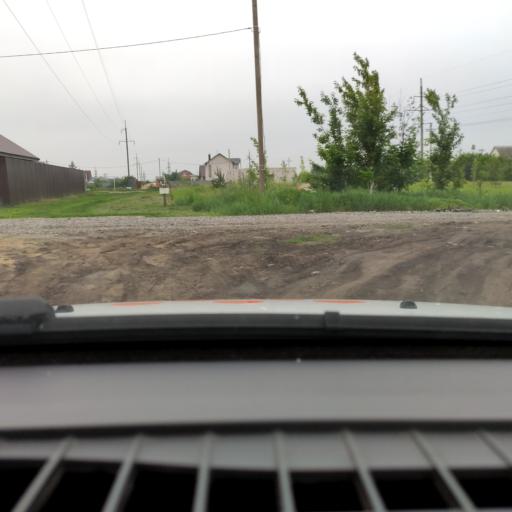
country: RU
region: Voronezj
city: Novaya Usman'
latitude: 51.6608
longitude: 39.4122
